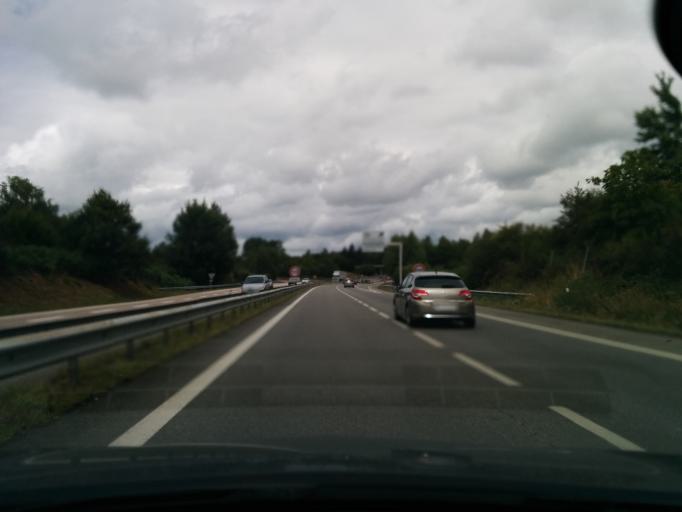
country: FR
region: Limousin
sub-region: Departement de la Haute-Vienne
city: Razes
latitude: 45.9855
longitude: 1.3254
